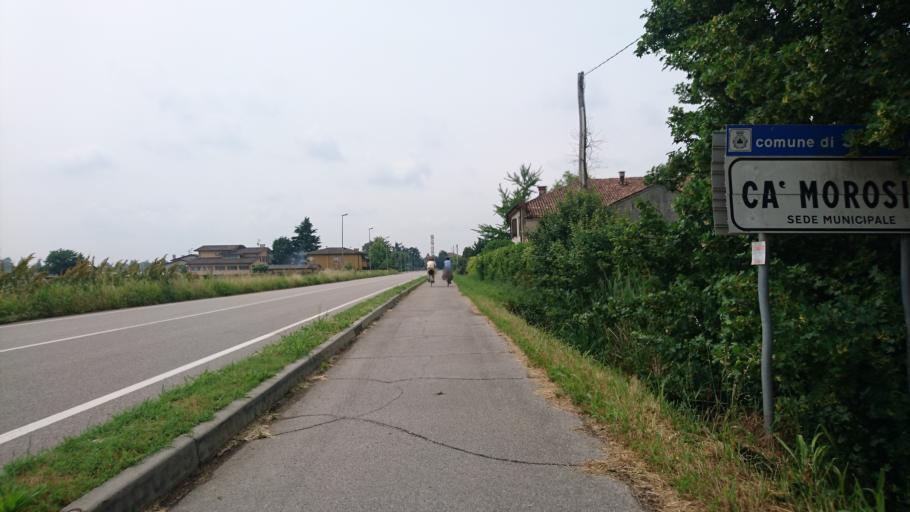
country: IT
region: Veneto
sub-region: Provincia di Rovigo
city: Lendinara
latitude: 45.1171
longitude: 11.6216
